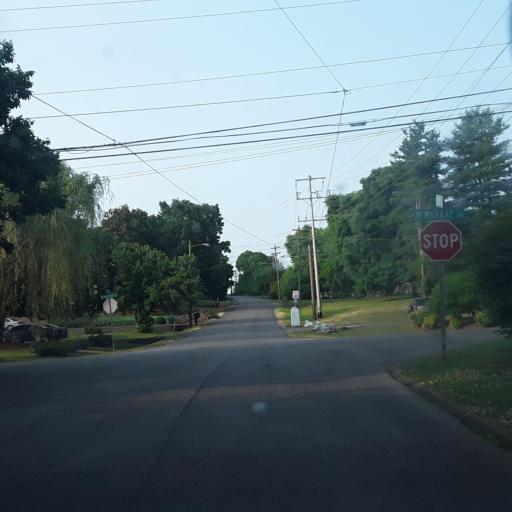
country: US
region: Tennessee
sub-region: Williamson County
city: Brentwood
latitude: 36.0553
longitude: -86.7319
